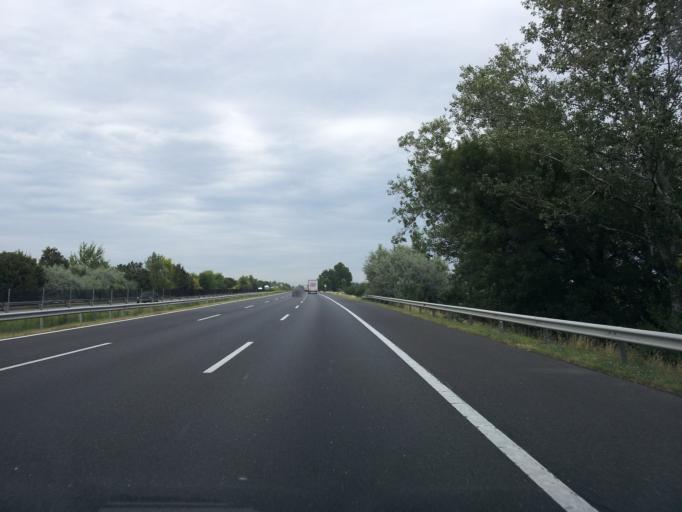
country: HU
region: Fejer
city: Kapolnasnyek
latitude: 47.2762
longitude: 18.7054
